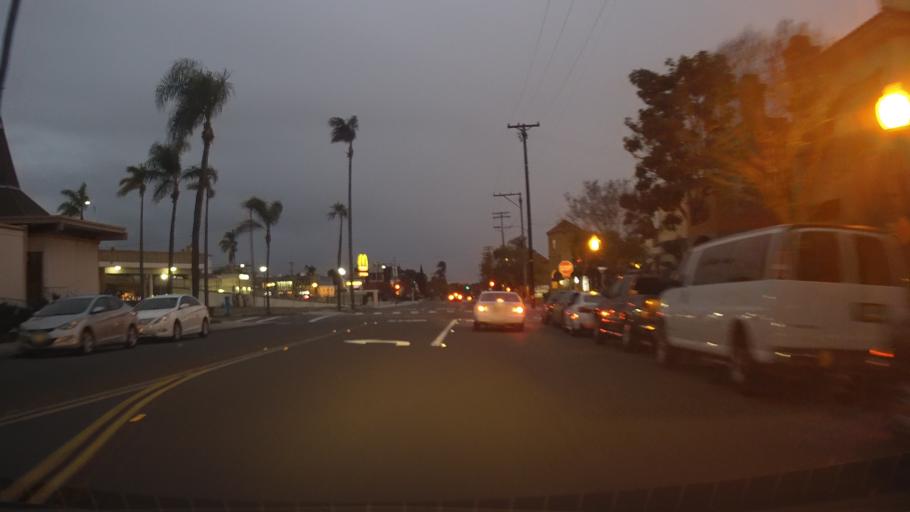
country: US
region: California
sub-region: San Diego County
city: San Diego
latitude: 32.7501
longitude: -117.1513
